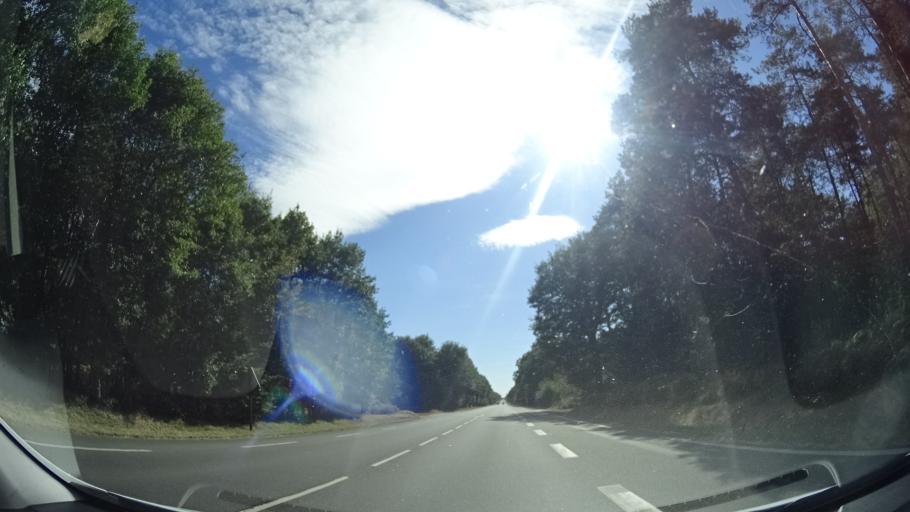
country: FR
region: Centre
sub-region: Departement du Loiret
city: Vitry-aux-Loges
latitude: 47.9257
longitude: 2.3301
